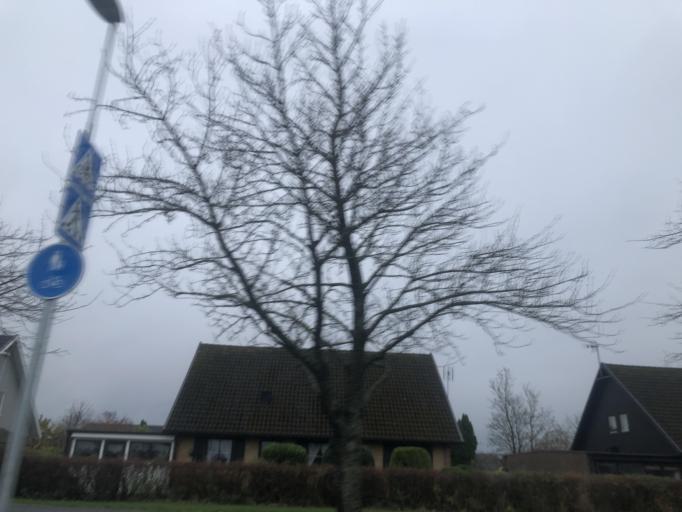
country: SE
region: Skane
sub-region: Trelleborgs Kommun
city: Trelleborg
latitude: 55.3887
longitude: 13.1641
